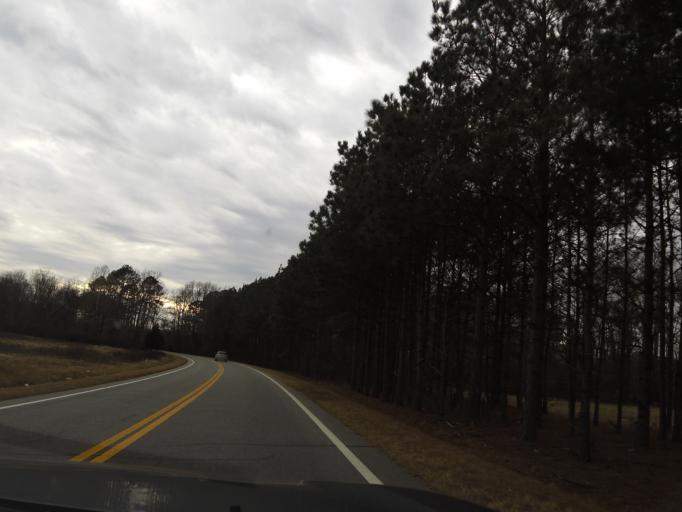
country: US
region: North Carolina
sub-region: Edgecombe County
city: Tarboro
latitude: 36.0097
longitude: -77.5367
